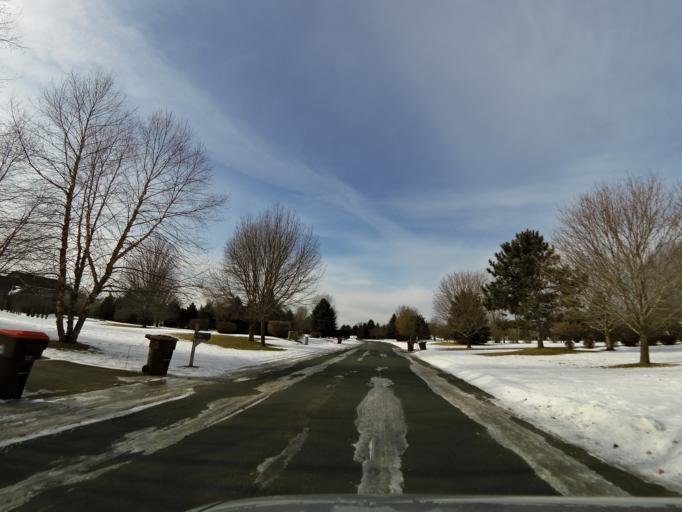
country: US
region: Minnesota
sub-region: Washington County
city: Lake Elmo
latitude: 44.9835
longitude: -92.8559
